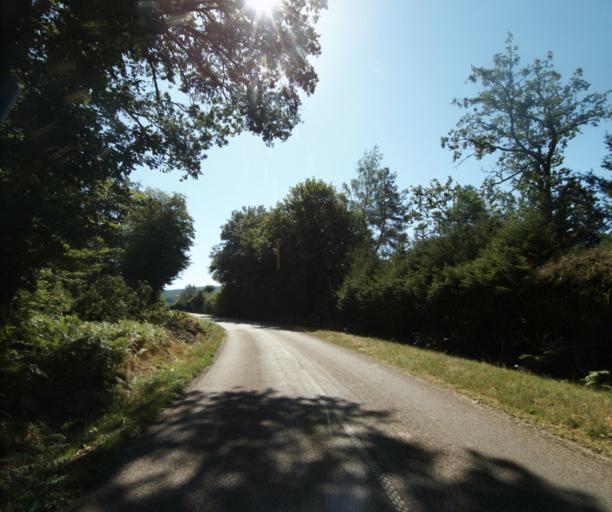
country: FR
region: Lorraine
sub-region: Departement des Vosges
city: Epinal
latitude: 48.1448
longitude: 6.4718
